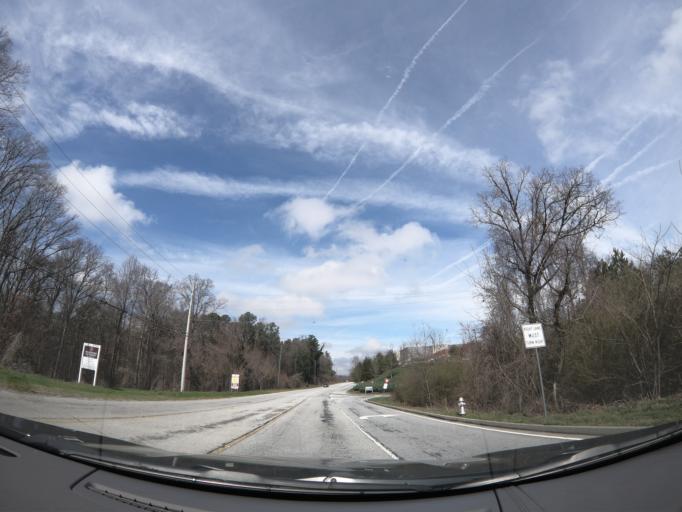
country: US
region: Georgia
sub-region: Fulton County
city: College Park
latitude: 33.6375
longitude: -84.4681
